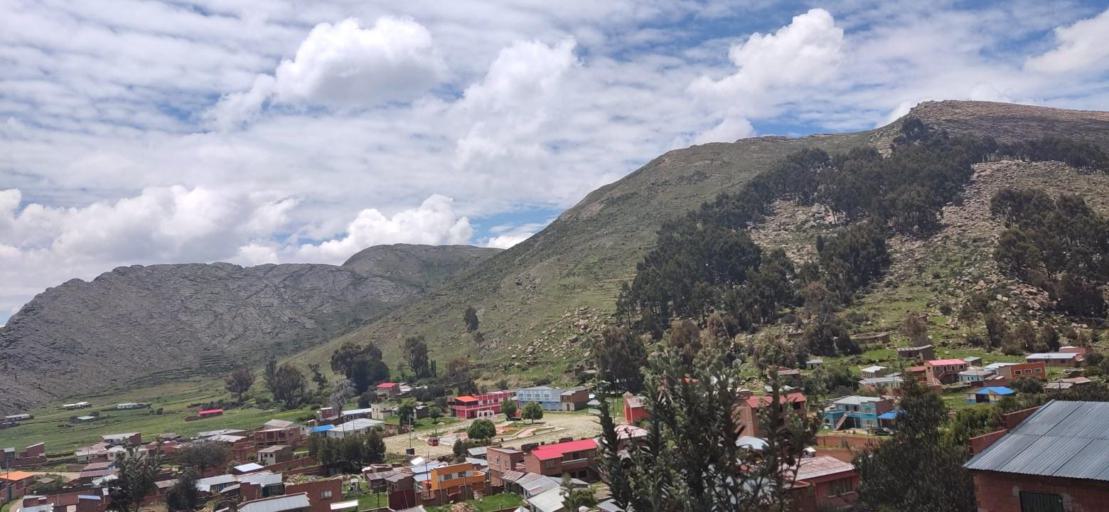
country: BO
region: La Paz
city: Batallas
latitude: -16.3446
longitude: -68.6391
